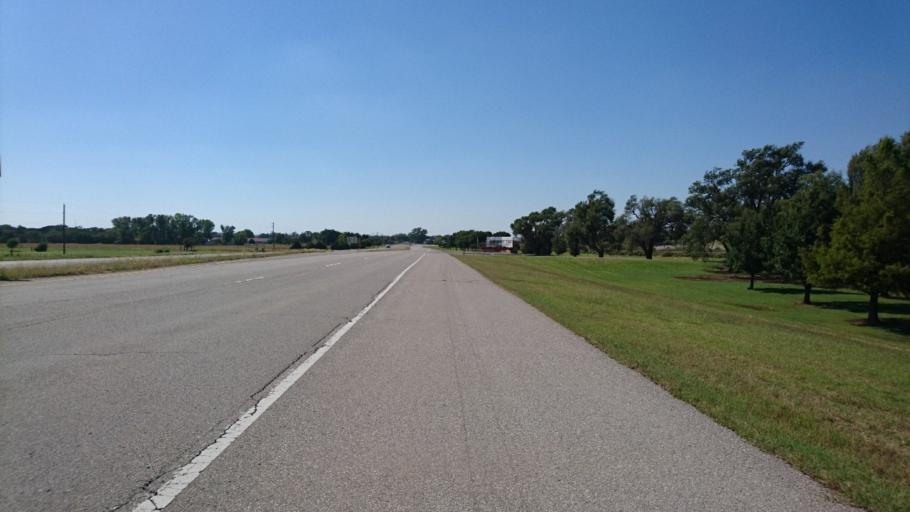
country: US
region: Oklahoma
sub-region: Custer County
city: Clinton
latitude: 35.5153
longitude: -98.9316
